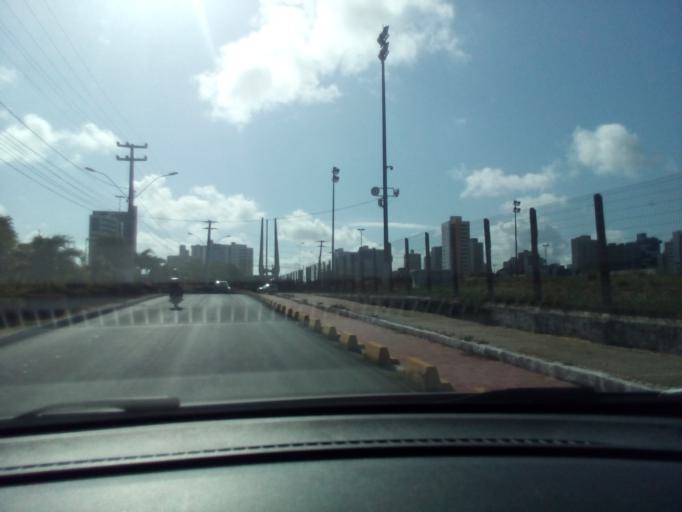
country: BR
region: Rio Grande do Norte
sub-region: Natal
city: Natal
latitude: -5.8382
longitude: -35.2097
